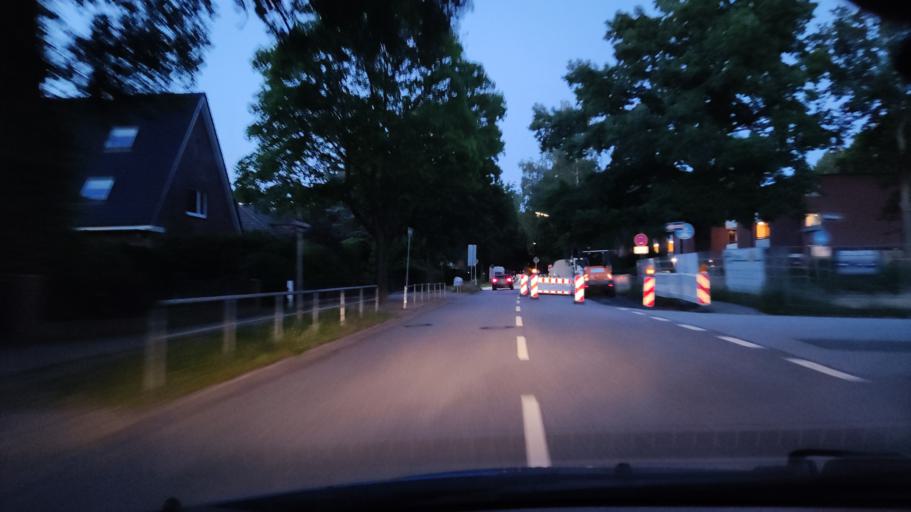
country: DE
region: Schleswig-Holstein
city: Wedel
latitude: 53.5771
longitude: 9.7600
